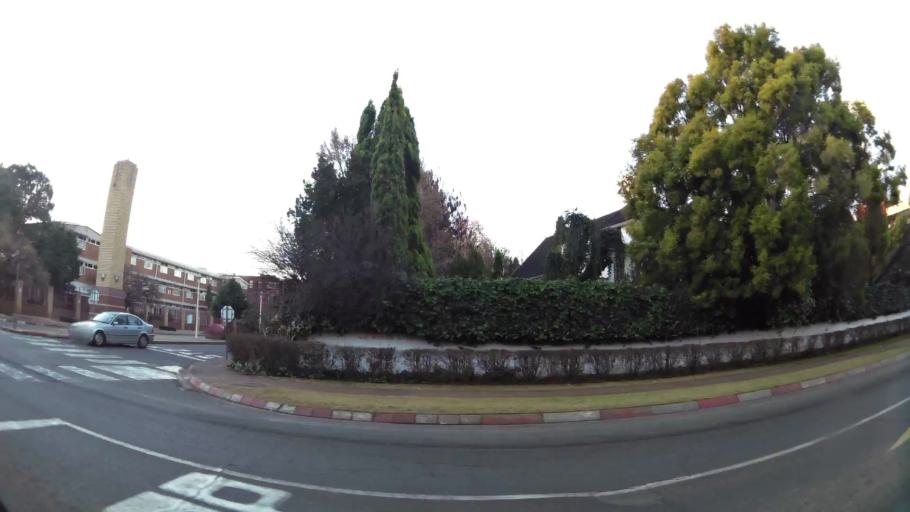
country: ZA
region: North-West
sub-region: Dr Kenneth Kaunda District Municipality
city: Potchefstroom
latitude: -26.6911
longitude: 27.0932
